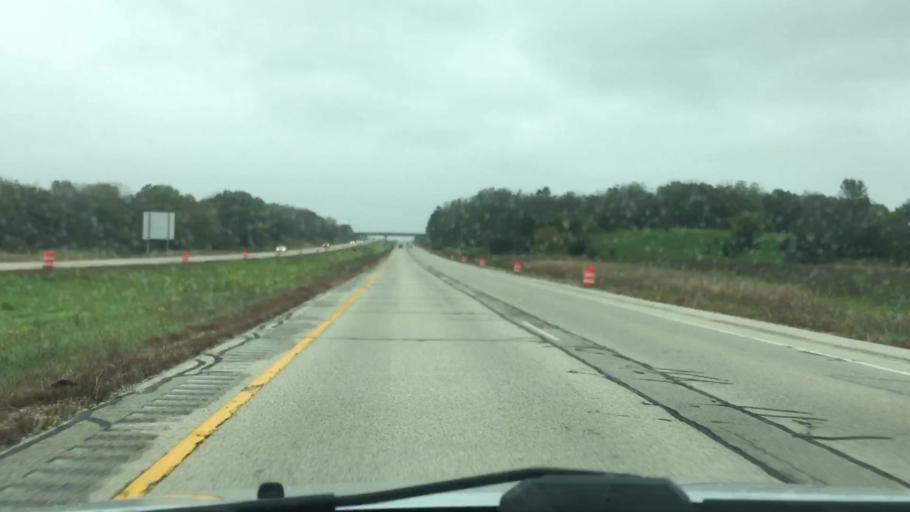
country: US
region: Wisconsin
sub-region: Walworth County
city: Lake Geneva
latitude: 42.5780
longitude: -88.3865
